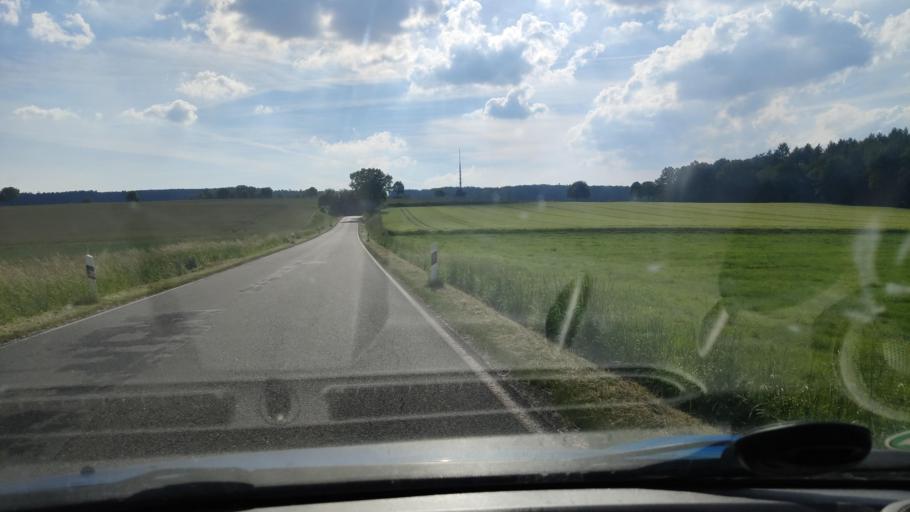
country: DE
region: Lower Saxony
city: Hardegsen
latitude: 51.7095
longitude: 9.7894
